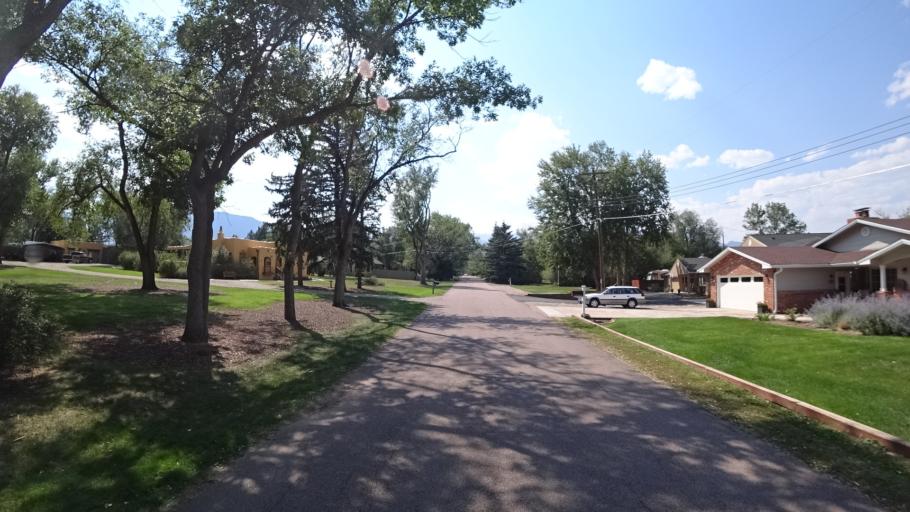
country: US
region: Colorado
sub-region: El Paso County
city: Colorado Springs
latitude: 38.7997
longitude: -104.8308
